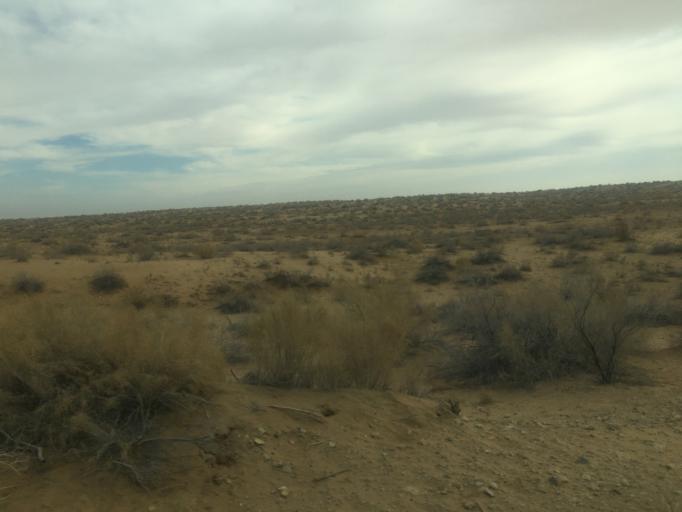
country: TM
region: Lebap
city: Gazojak
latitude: 40.3841
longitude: 61.1903
